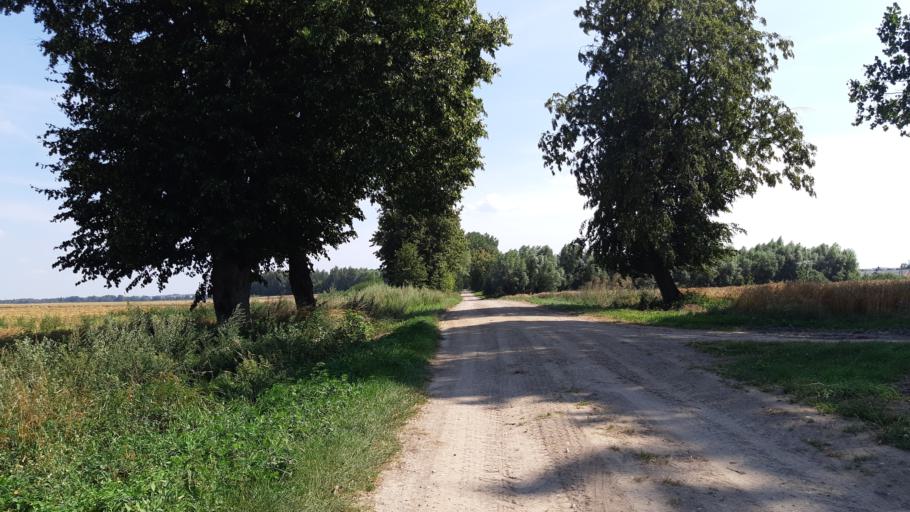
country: LT
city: Virbalis
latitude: 54.6400
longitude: 22.8211
